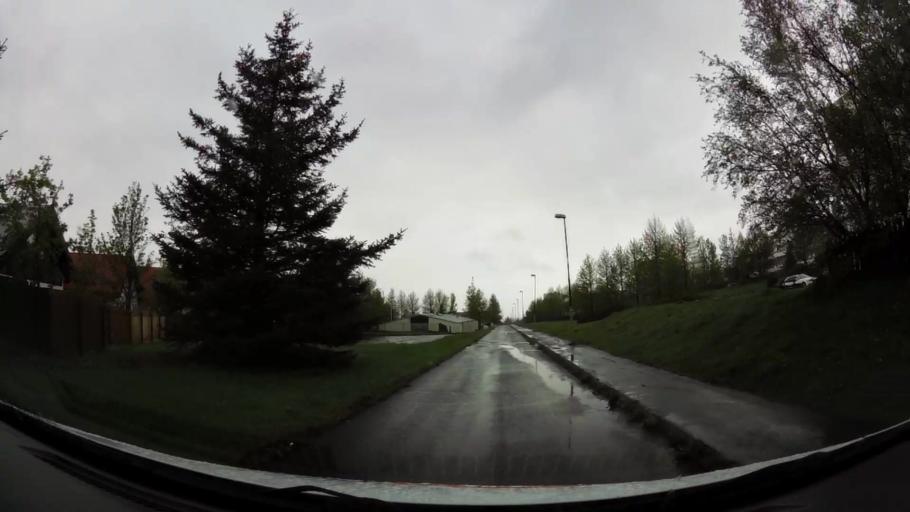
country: IS
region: Capital Region
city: Reykjavik
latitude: 64.0971
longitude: -21.8372
